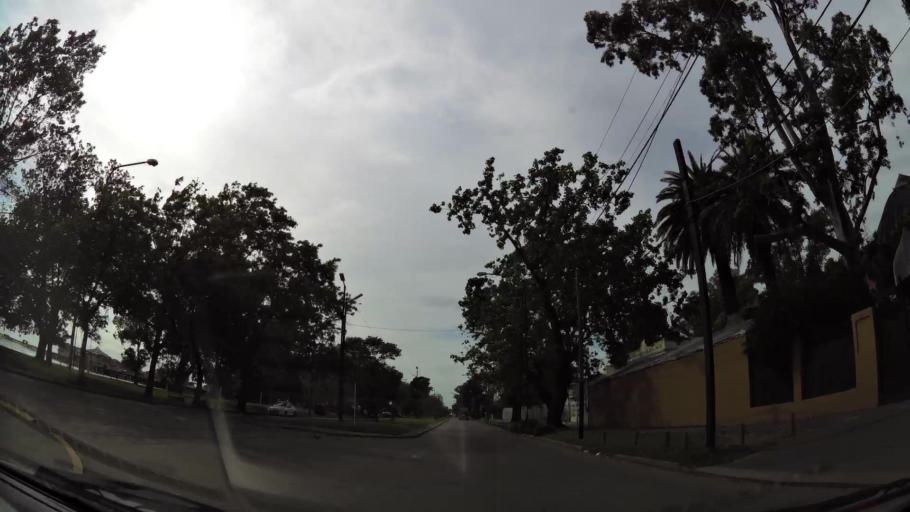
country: AR
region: Buenos Aires
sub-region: Partido de Quilmes
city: Quilmes
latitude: -34.7095
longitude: -58.2249
